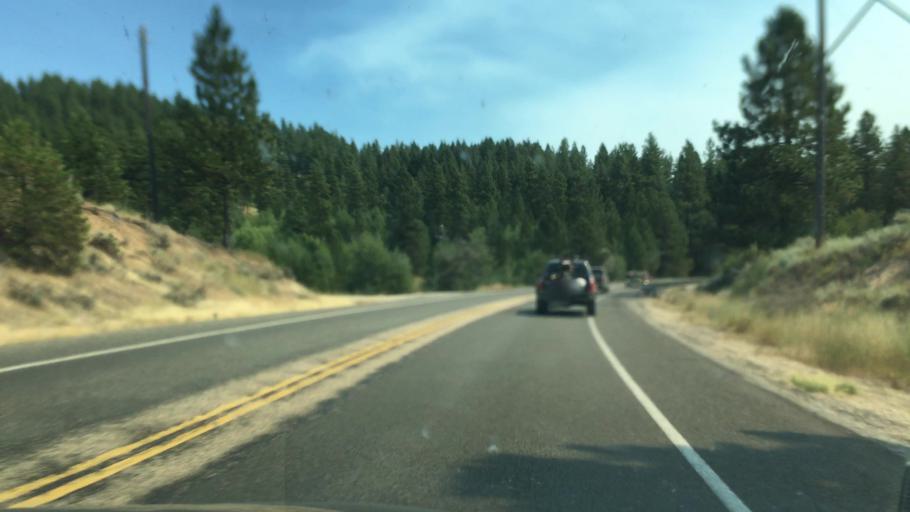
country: US
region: Idaho
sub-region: Valley County
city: Cascade
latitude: 44.5952
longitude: -116.0419
